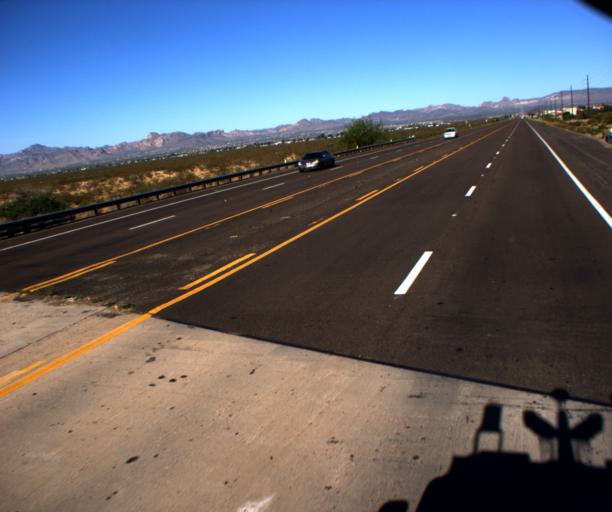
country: US
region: Arizona
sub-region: Mohave County
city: Golden Valley
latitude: 35.2211
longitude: -114.1953
